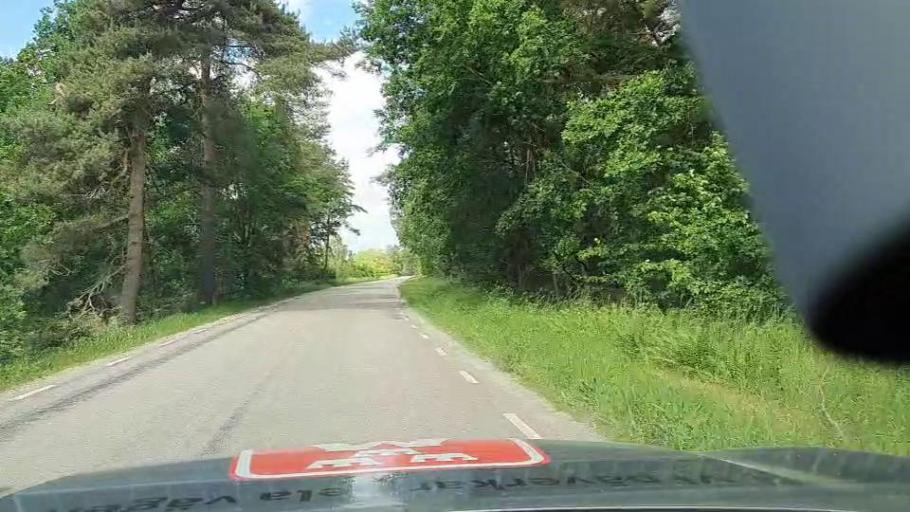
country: SE
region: Blekinge
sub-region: Karlshamns Kommun
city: Morrum
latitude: 56.1027
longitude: 14.6854
